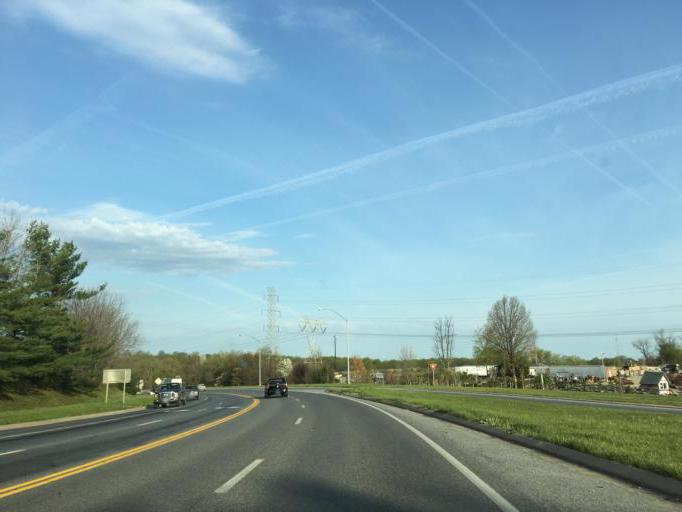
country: US
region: Maryland
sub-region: Baltimore County
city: Reisterstown
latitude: 39.4758
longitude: -76.8294
